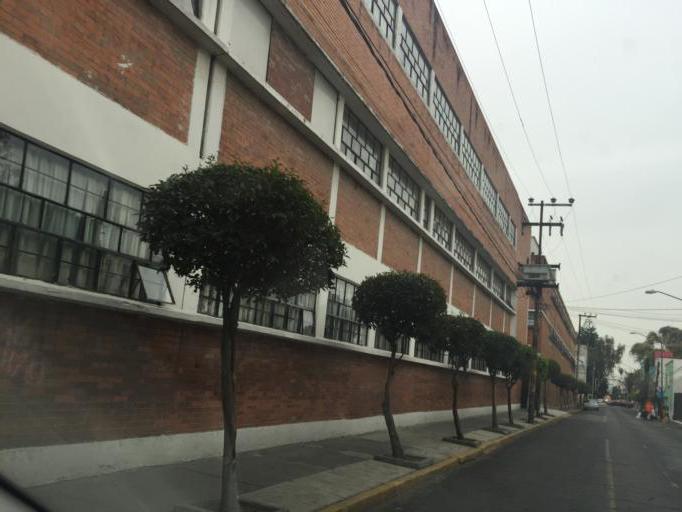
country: MX
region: Mexico
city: Colonia Lindavista
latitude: 19.4925
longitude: -99.1239
